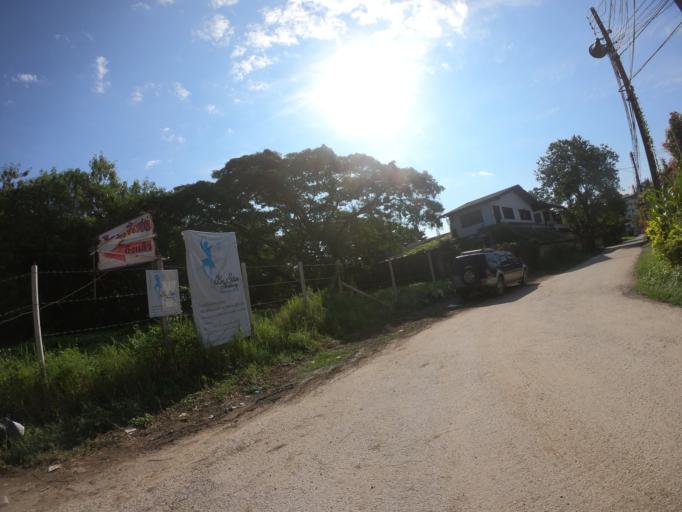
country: TH
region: Chiang Mai
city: Chiang Mai
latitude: 18.8090
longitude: 98.9935
